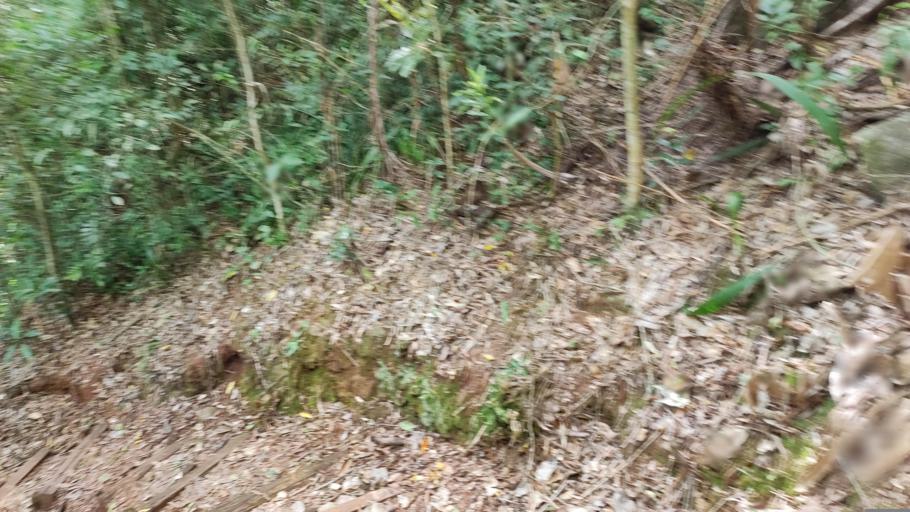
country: AR
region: Misiones
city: Dos de Mayo
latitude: -26.9977
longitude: -54.6247
